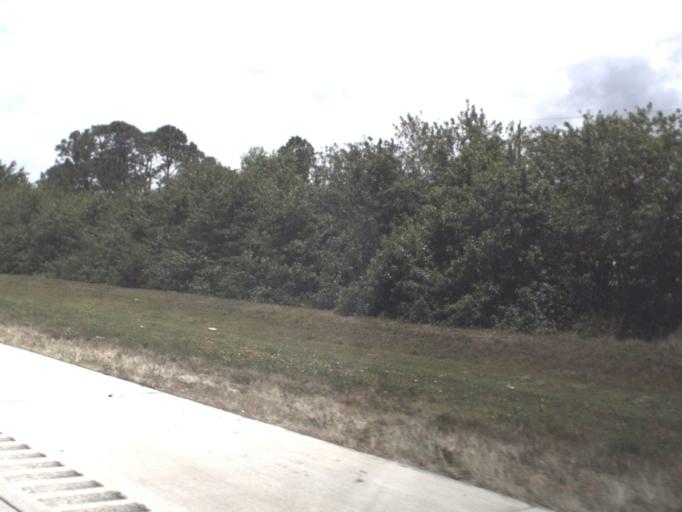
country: US
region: Florida
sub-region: Brevard County
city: Cocoa West
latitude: 28.3526
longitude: -80.7900
